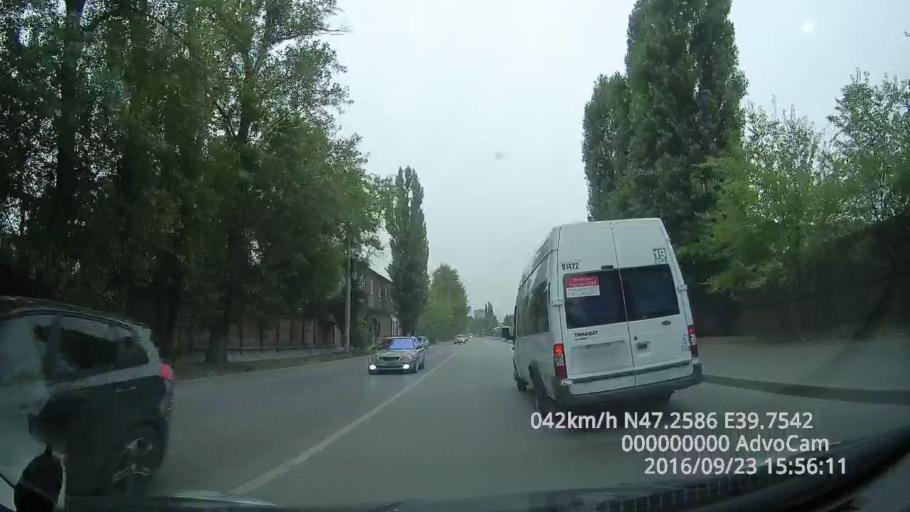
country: RU
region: Rostov
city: Imeni Chkalova
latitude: 47.2586
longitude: 39.7542
